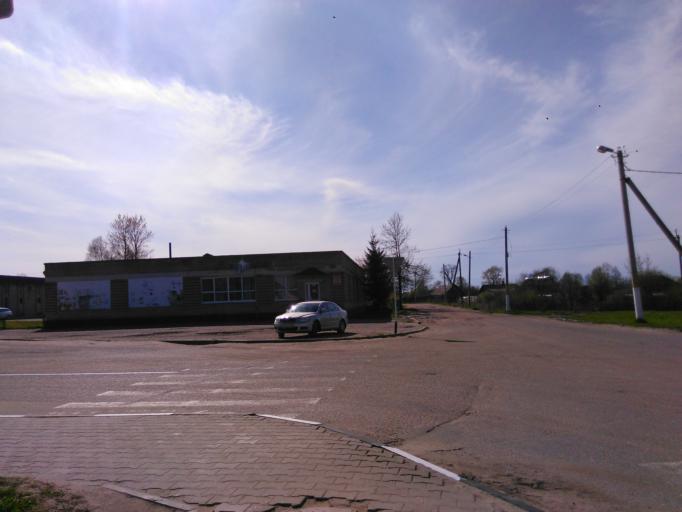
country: BY
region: Vitebsk
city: Chashniki
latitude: 54.8594
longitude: 29.1587
